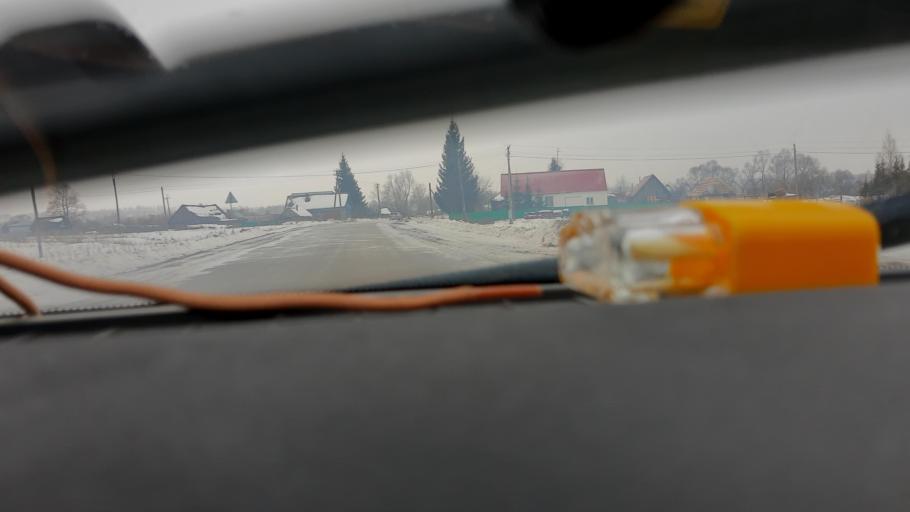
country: RU
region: Bashkortostan
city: Ulukulevo
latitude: 54.5136
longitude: 56.4133
